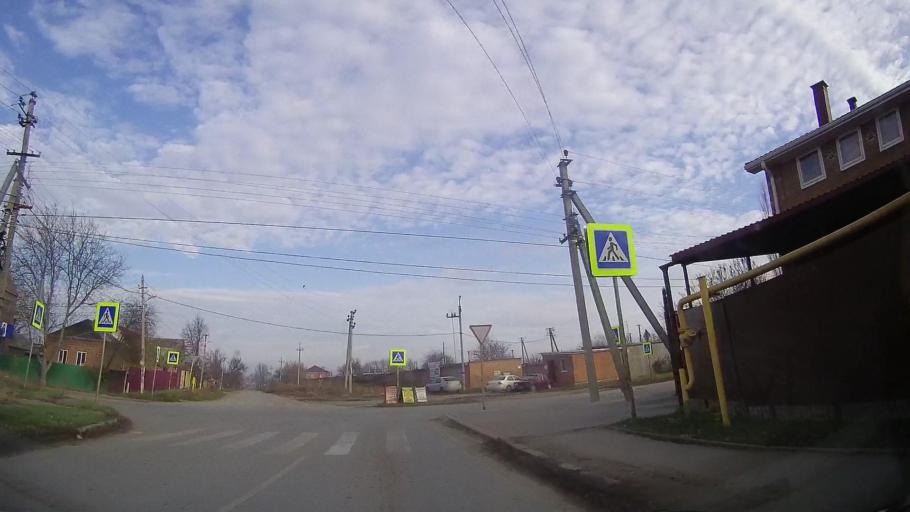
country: RU
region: Rostov
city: Bataysk
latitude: 47.1303
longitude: 39.7846
